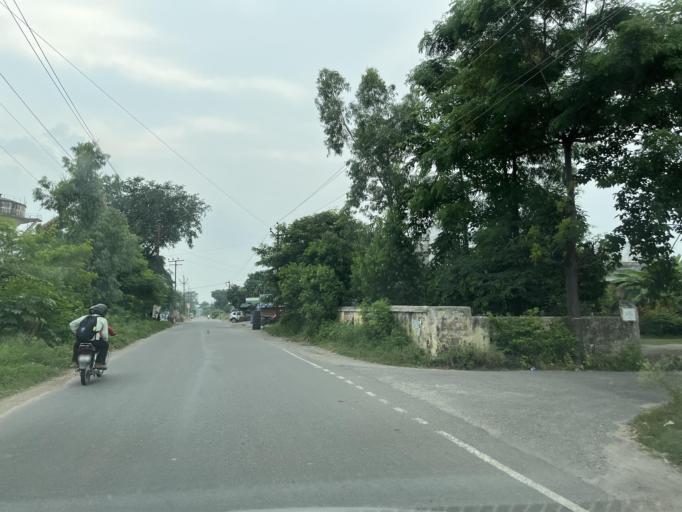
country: IN
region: Uttarakhand
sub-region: Naini Tal
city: Haldwani
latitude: 29.1739
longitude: 79.4760
